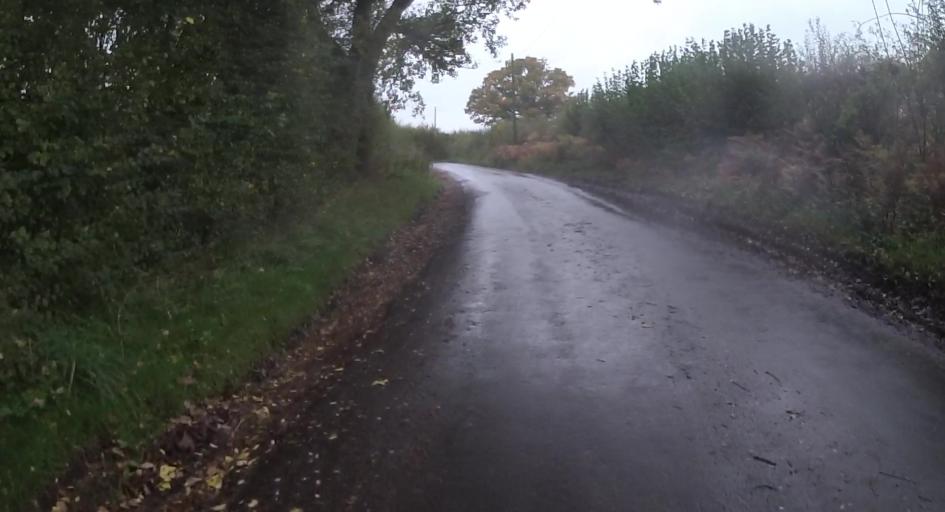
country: GB
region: England
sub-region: Surrey
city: Farnham
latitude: 51.2021
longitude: -0.8503
